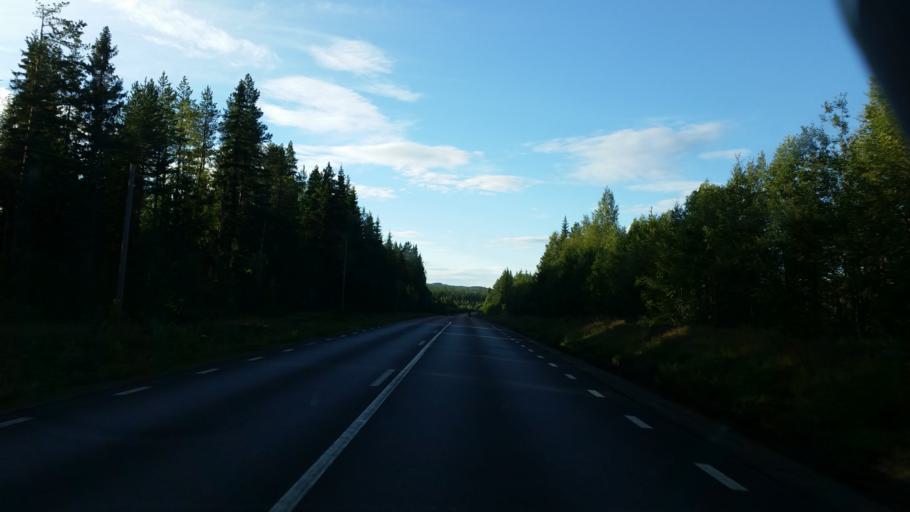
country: SE
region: Vaesterbotten
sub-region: Dorotea Kommun
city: Dorotea
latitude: 64.2028
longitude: 16.2868
